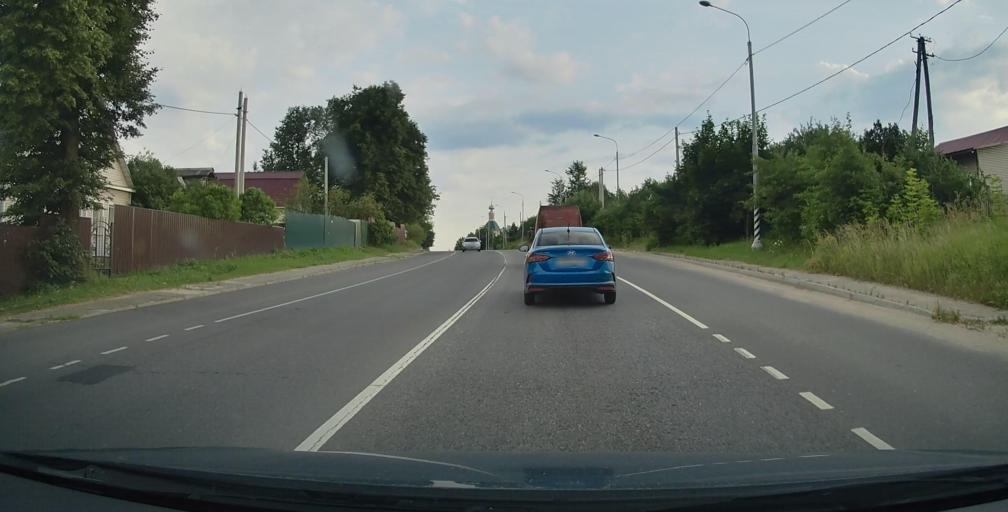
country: RU
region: Moskovskaya
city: Shemetovo
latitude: 56.4535
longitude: 38.1014
